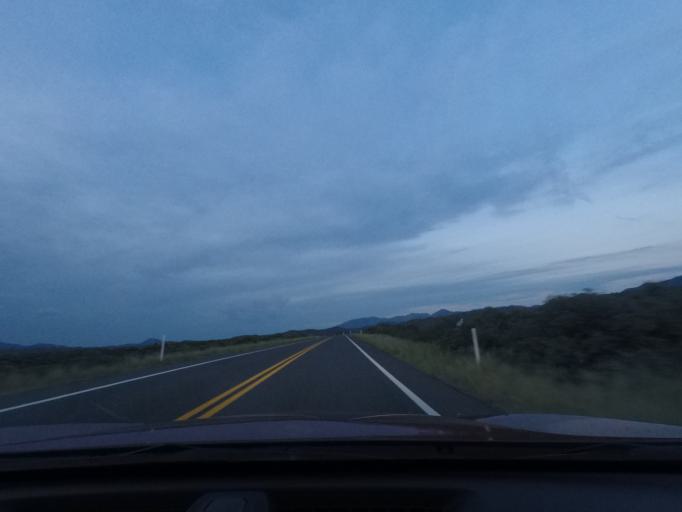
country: US
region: Arizona
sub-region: Yavapai County
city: Williamson
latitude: 34.5393
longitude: -112.6806
